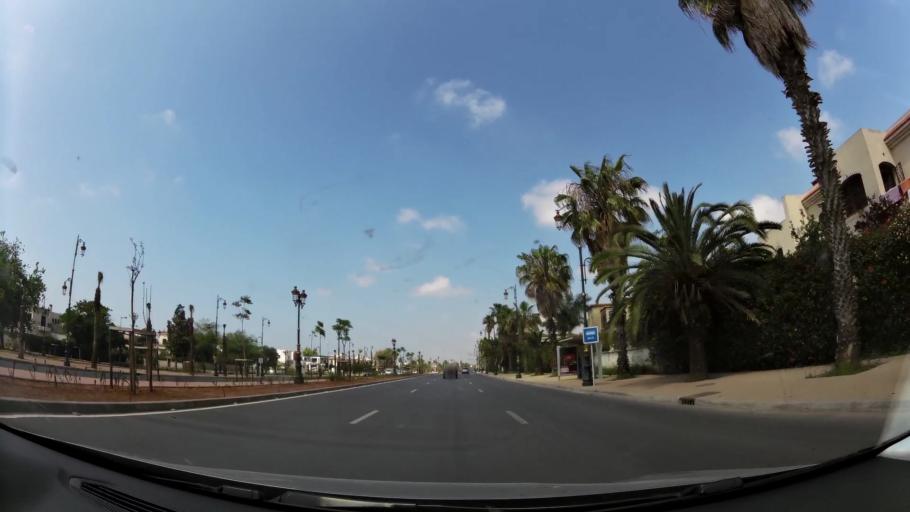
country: MA
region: Rabat-Sale-Zemmour-Zaer
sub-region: Skhirate-Temara
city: Temara
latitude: 33.9553
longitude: -6.8795
